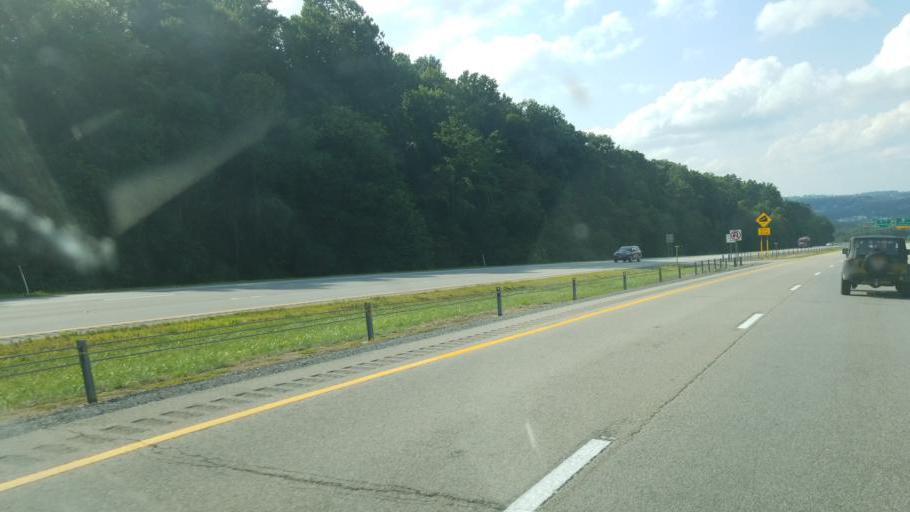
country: US
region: West Virginia
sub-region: Monongalia County
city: Cheat Lake
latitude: 39.6631
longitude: -79.8449
